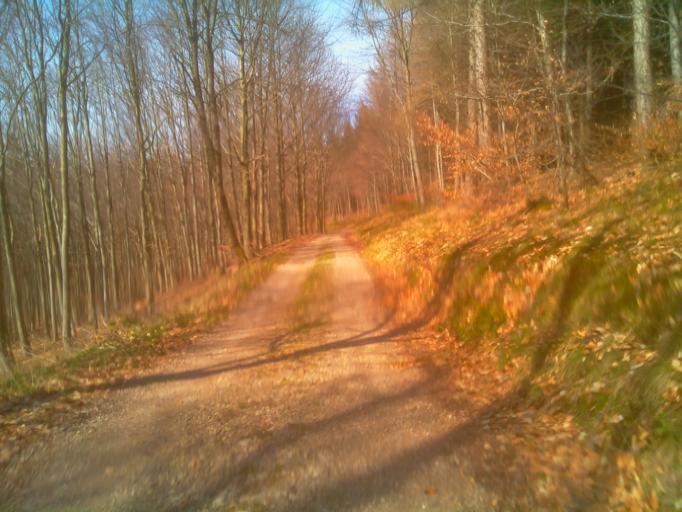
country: DE
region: Baden-Wuerttemberg
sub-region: Karlsruhe Region
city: Wilhelmsfeld
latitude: 49.4561
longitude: 8.7557
